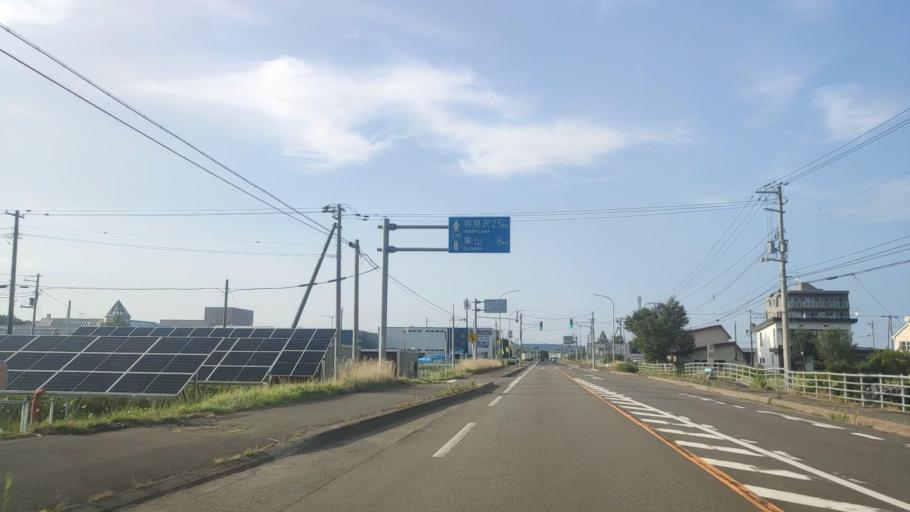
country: JP
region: Hokkaido
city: Iwamizawa
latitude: 43.0097
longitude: 141.7893
